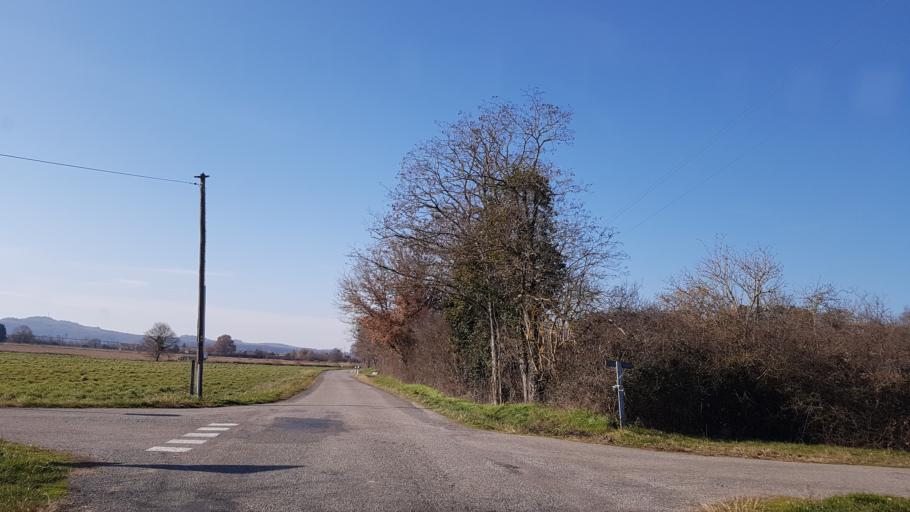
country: FR
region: Midi-Pyrenees
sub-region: Departement de l'Ariege
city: Mazeres
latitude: 43.1832
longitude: 1.6472
